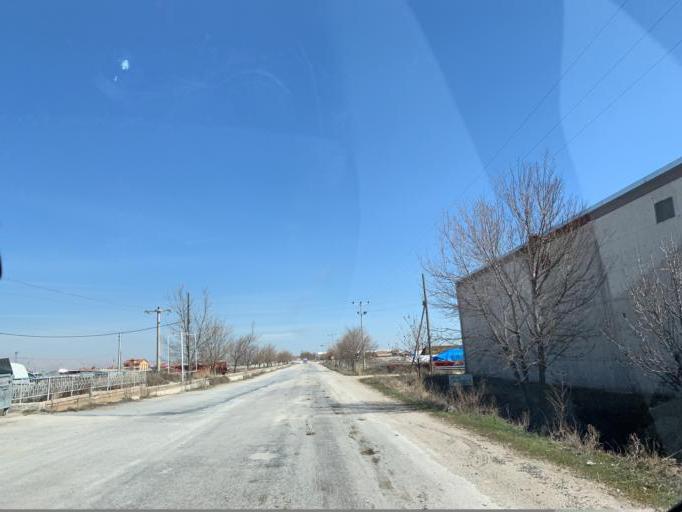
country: TR
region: Konya
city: Yarma
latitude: 37.7485
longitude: 32.8383
